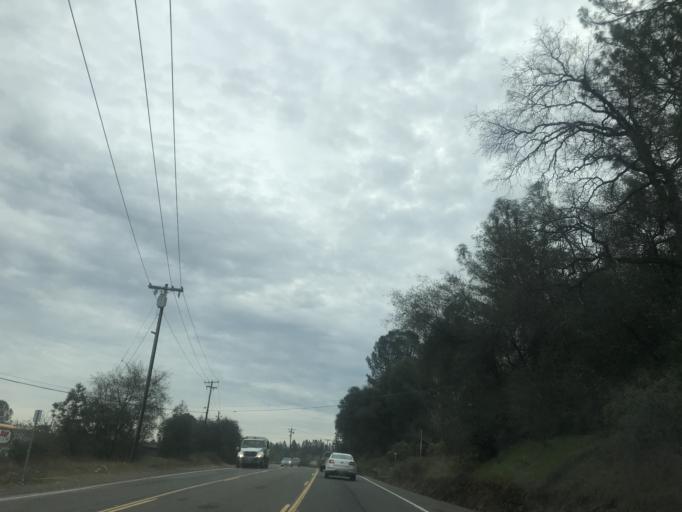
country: US
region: California
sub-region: El Dorado County
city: Diamond Springs
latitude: 38.7032
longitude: -120.8257
